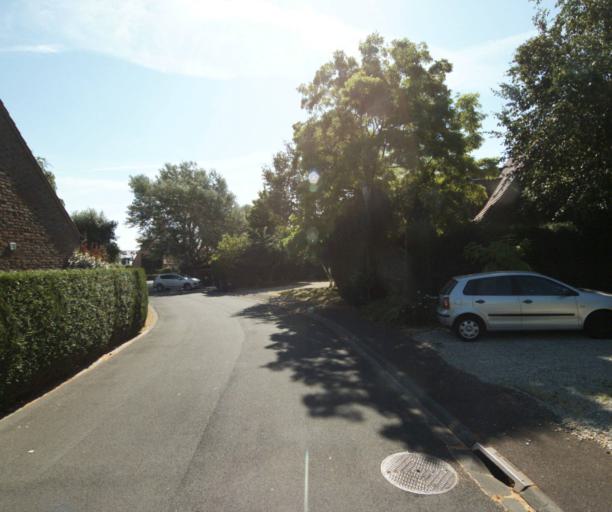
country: FR
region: Nord-Pas-de-Calais
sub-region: Departement du Nord
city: Marcq-en-Baroeul
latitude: 50.6779
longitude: 3.0983
